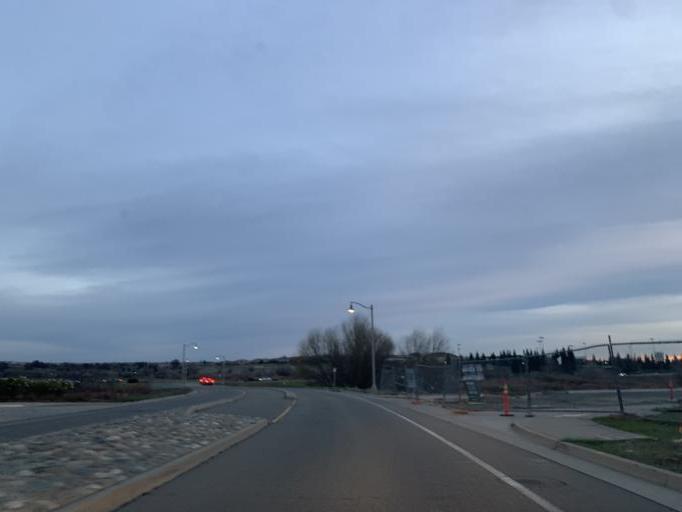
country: US
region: California
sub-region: Placer County
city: Lincoln
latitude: 38.8491
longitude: -121.2877
